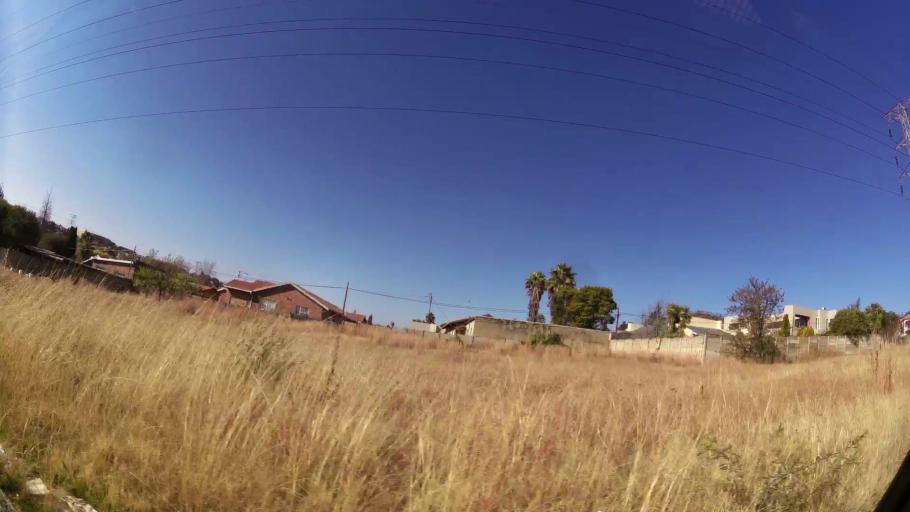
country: ZA
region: Gauteng
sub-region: City of Johannesburg Metropolitan Municipality
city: Johannesburg
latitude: -26.2777
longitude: 28.0240
